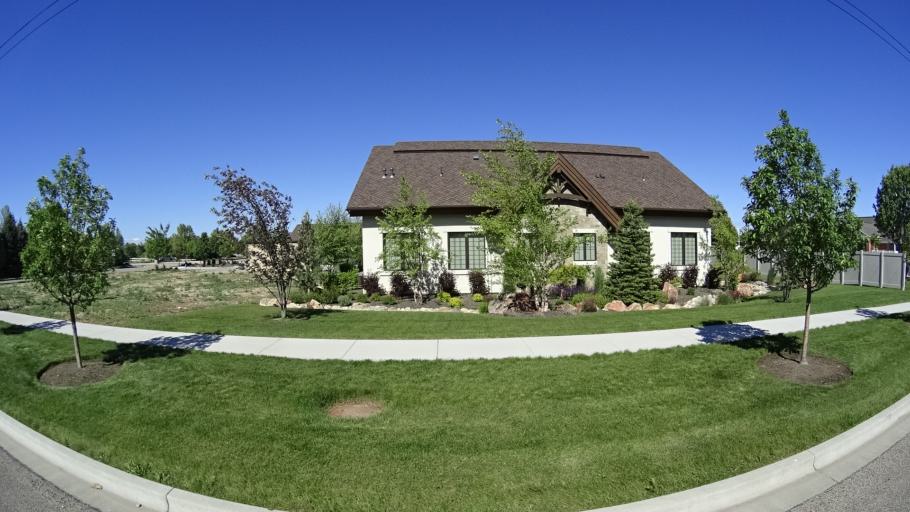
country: US
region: Idaho
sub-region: Ada County
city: Eagle
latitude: 43.6645
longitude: -116.3936
